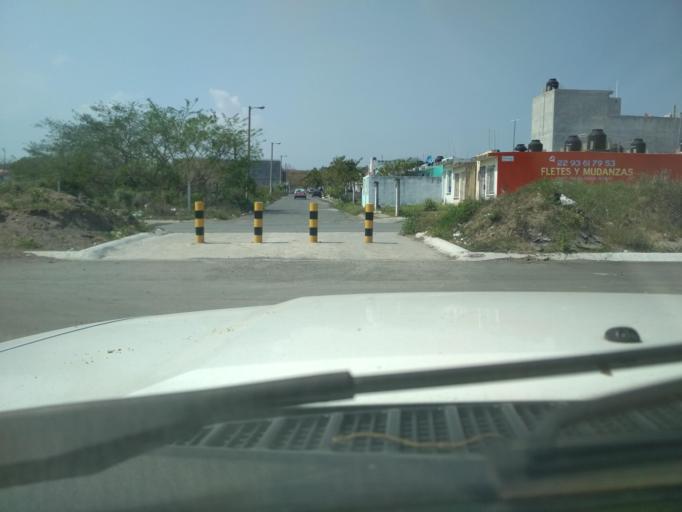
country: MX
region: Veracruz
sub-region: Veracruz
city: Lomas de Rio Medio Cuatro
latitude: 19.1921
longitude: -96.2085
